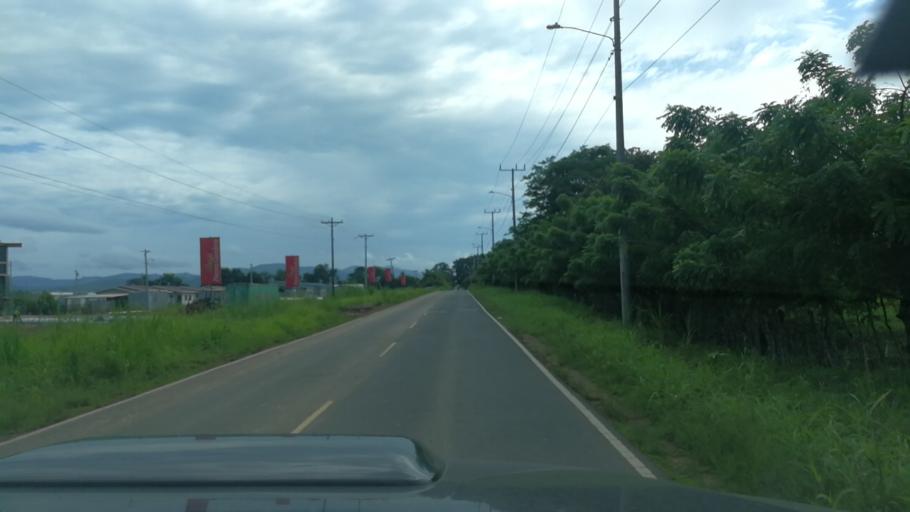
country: PA
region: Panama
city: Paso Blanco
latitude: 9.1098
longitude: -79.2667
